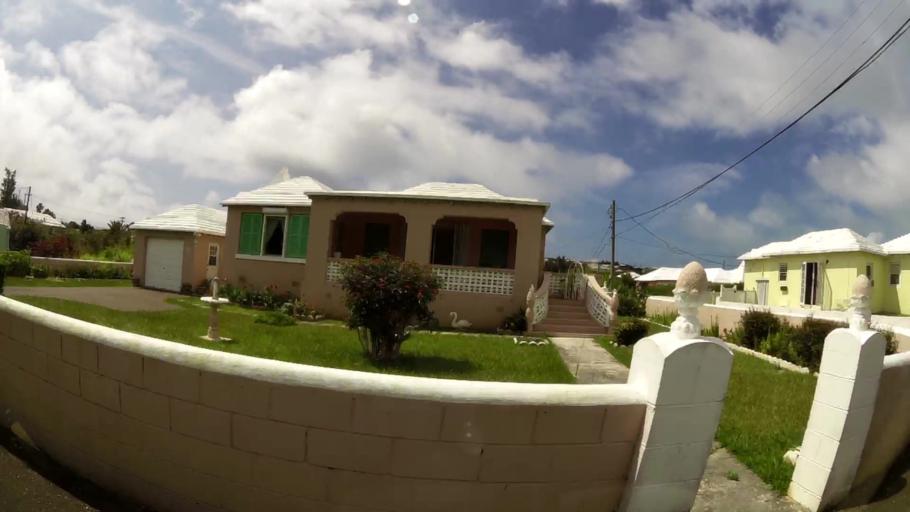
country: BM
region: Saint George
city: Saint George
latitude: 32.3708
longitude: -64.6539
